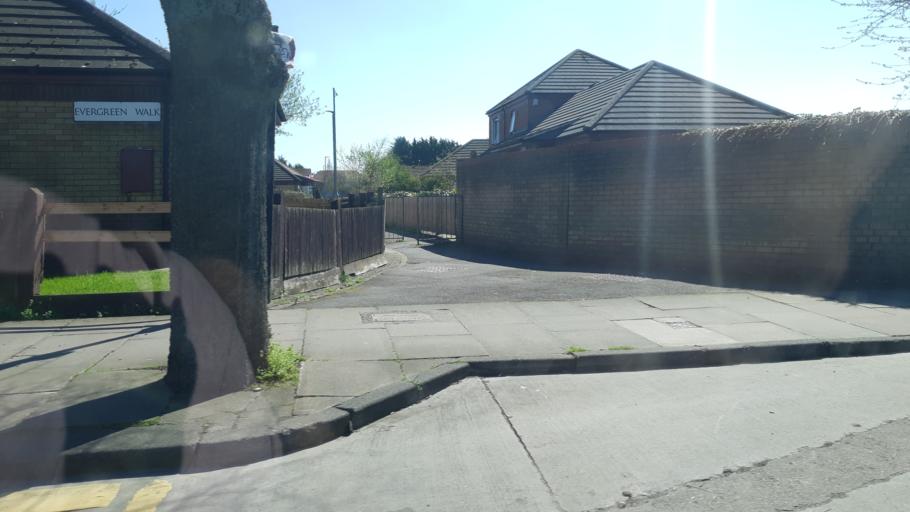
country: GB
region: England
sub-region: Middlesbrough
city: Middlesbrough
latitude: 54.5533
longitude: -1.2326
